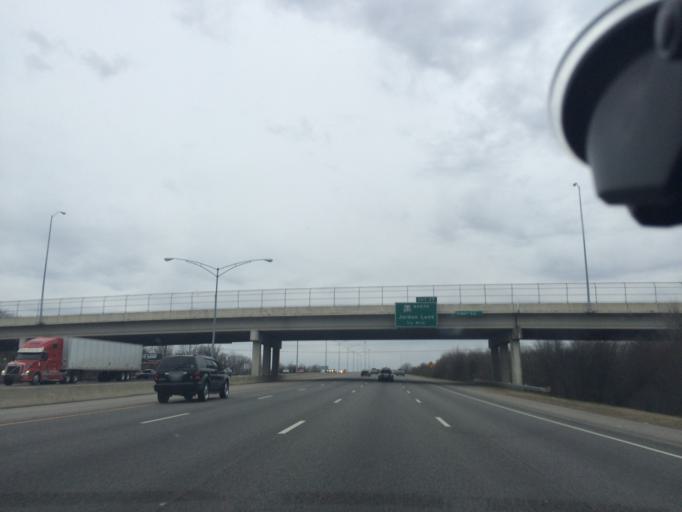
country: US
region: Alabama
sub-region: Madison County
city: Huntsville
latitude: 34.7252
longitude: -86.6084
